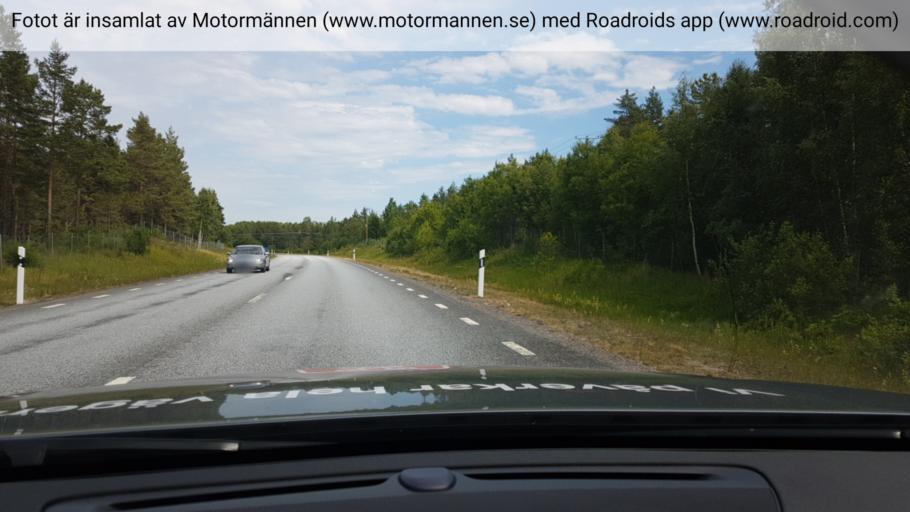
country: SE
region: Uppsala
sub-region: Osthammars Kommun
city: Anneberg
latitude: 60.1718
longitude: 18.3906
